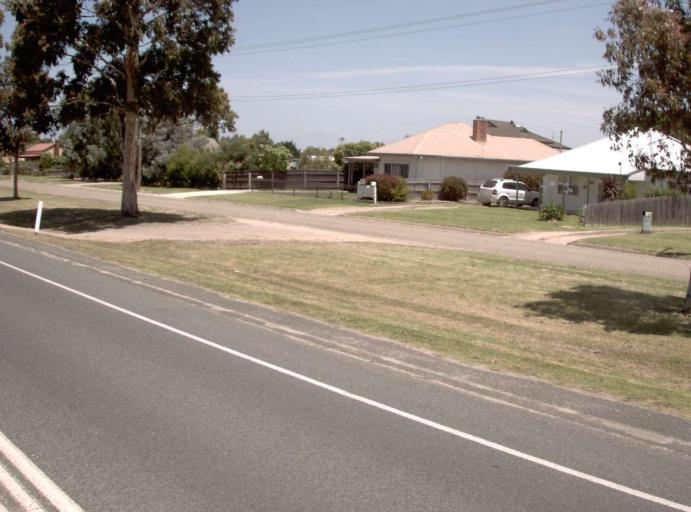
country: AU
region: Victoria
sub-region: East Gippsland
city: Bairnsdale
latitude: -37.8150
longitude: 147.6481
